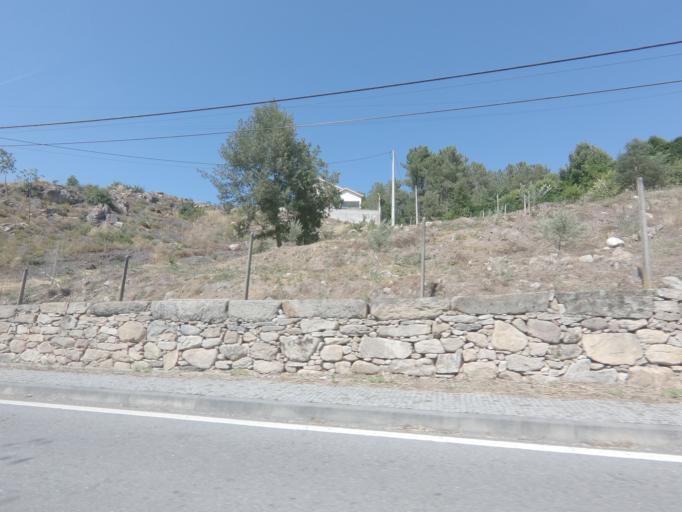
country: PT
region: Viseu
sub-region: Tarouca
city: Tarouca
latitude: 41.0251
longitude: -7.7537
